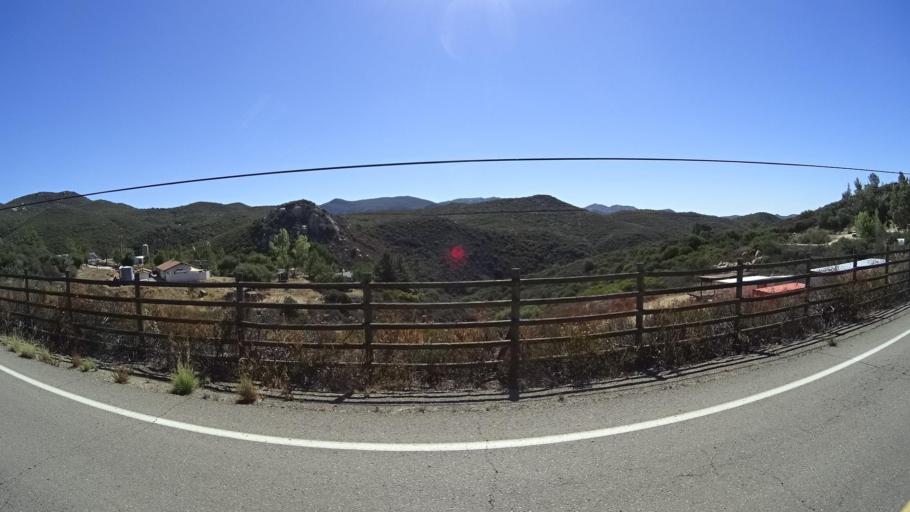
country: US
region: California
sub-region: San Diego County
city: Descanso
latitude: 32.8044
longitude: -116.6411
